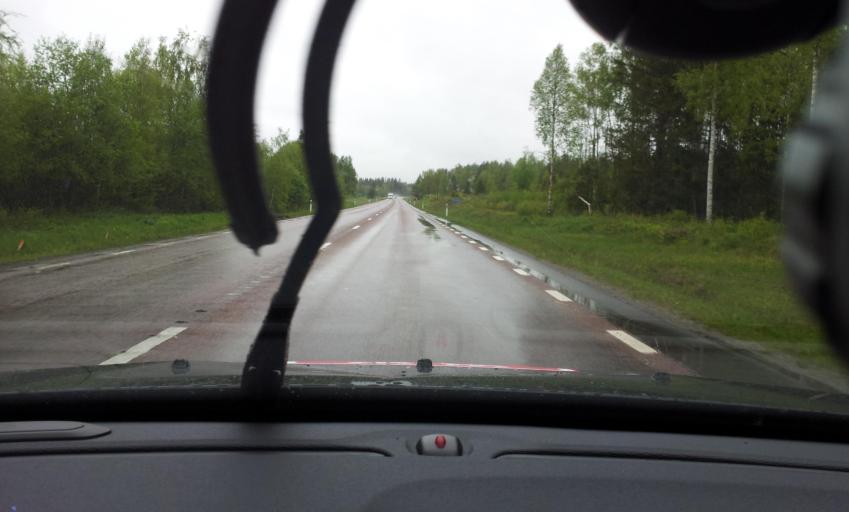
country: SE
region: Jaemtland
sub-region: Bergs Kommun
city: Hoverberg
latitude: 62.8951
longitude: 14.5242
